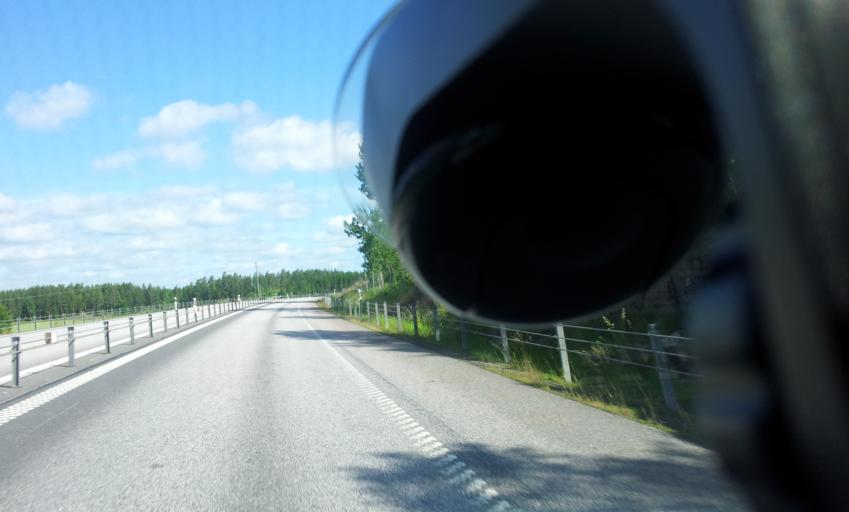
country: SE
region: OEstergoetland
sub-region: Soderkopings Kommun
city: Soederkoeping
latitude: 58.4014
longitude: 16.4036
